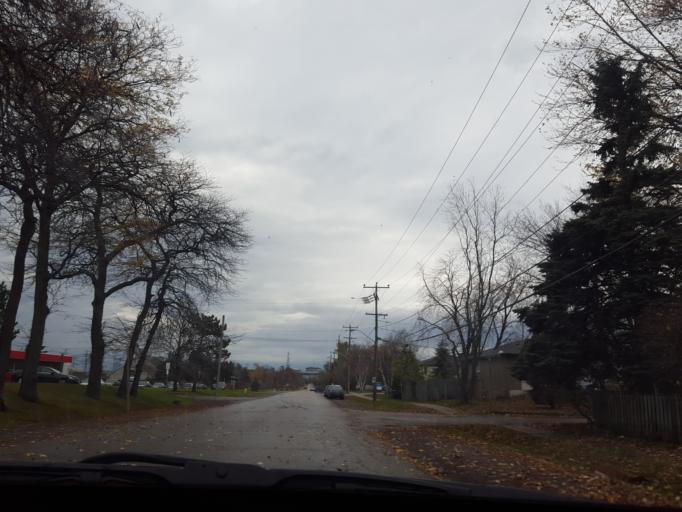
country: CA
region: Ontario
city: Ajax
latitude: 43.8300
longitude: -79.0769
